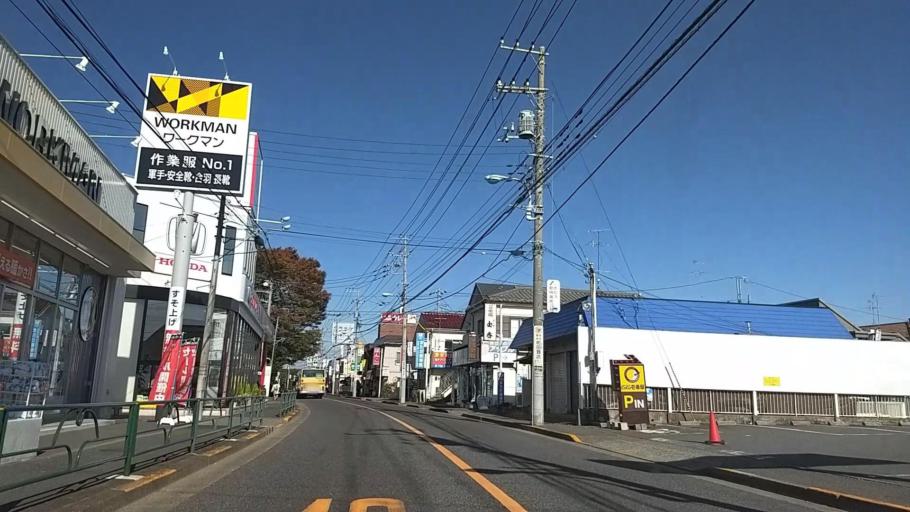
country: JP
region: Tokyo
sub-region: Machida-shi
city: Machida
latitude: 35.5311
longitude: 139.4618
